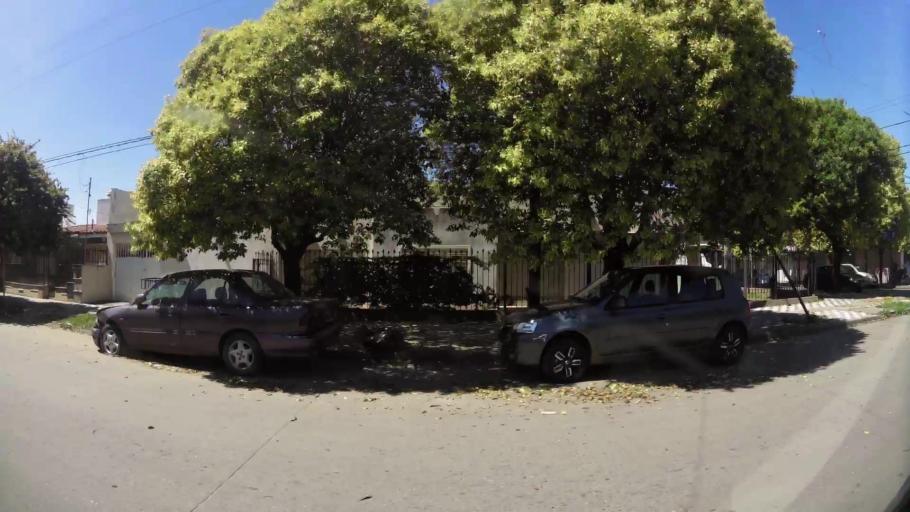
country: AR
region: Cordoba
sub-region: Departamento de Capital
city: Cordoba
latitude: -31.3859
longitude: -64.1606
